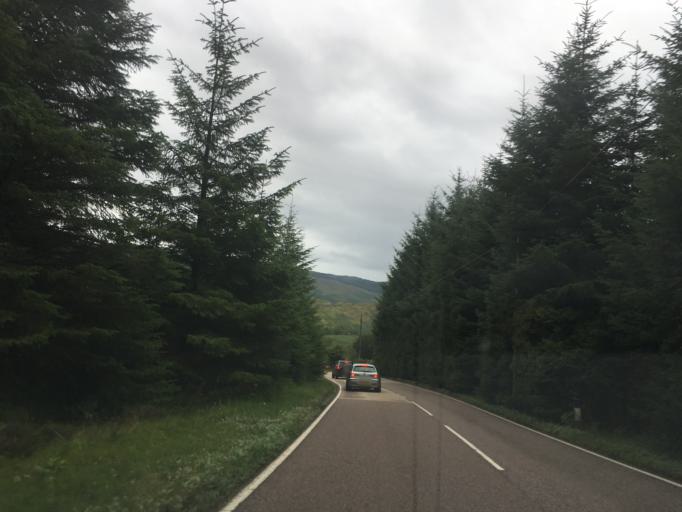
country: GB
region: Scotland
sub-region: Argyll and Bute
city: Oban
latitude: 56.2799
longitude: -5.4840
